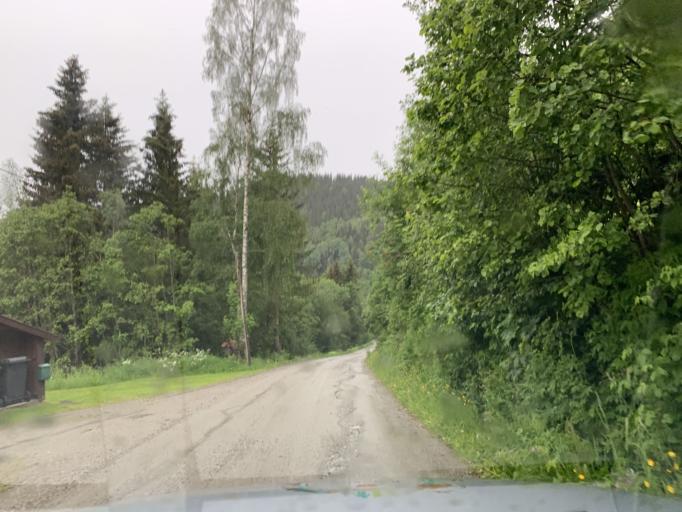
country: NO
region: Oppland
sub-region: Oyer
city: Tretten
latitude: 61.3906
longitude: 10.2774
